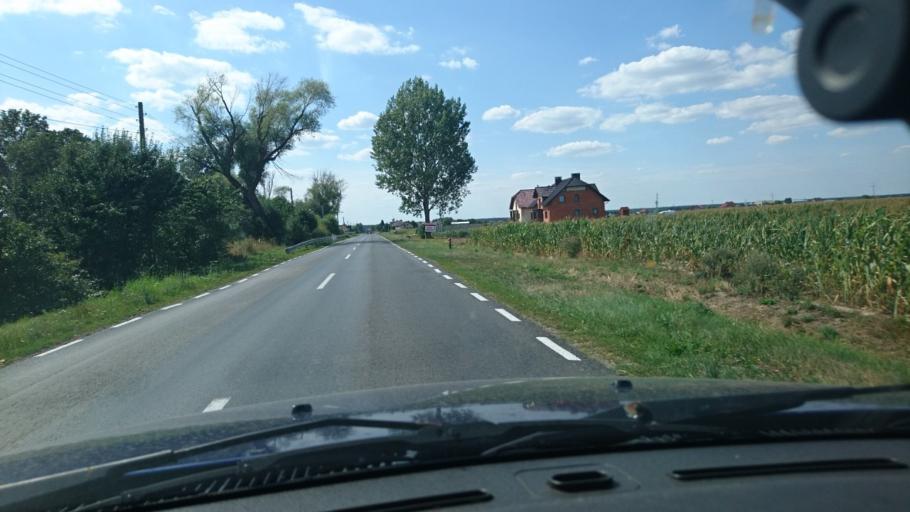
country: PL
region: Greater Poland Voivodeship
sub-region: Powiat krotoszynski
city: Sulmierzyce
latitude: 51.6053
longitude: 17.5502
